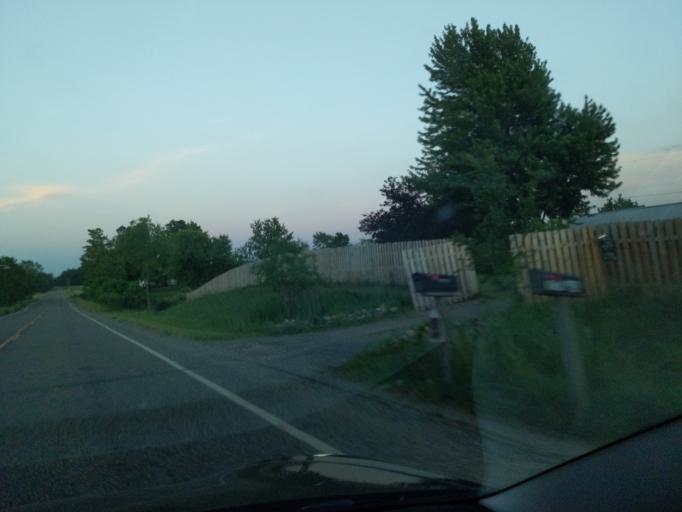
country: US
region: Michigan
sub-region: Barry County
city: Nashville
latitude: 42.5382
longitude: -85.0405
